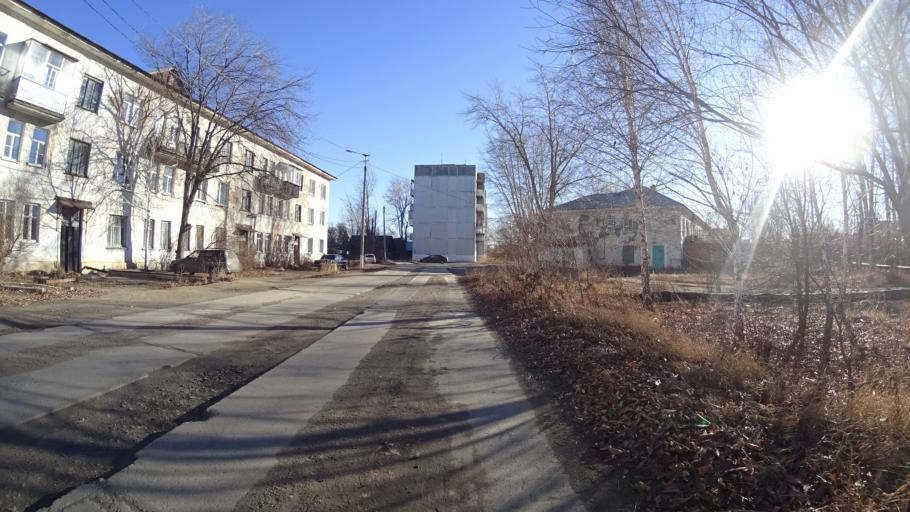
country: RU
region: Chelyabinsk
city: Troitsk
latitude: 54.1090
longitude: 61.5539
